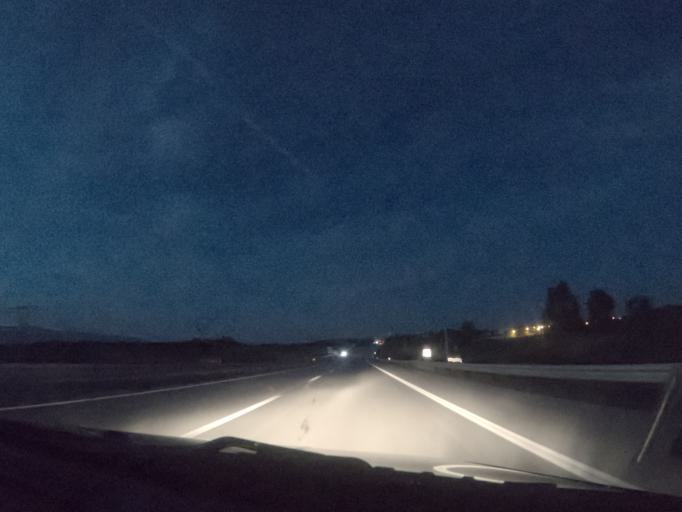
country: PT
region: Guarda
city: Alcains
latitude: 39.9331
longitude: -7.4660
